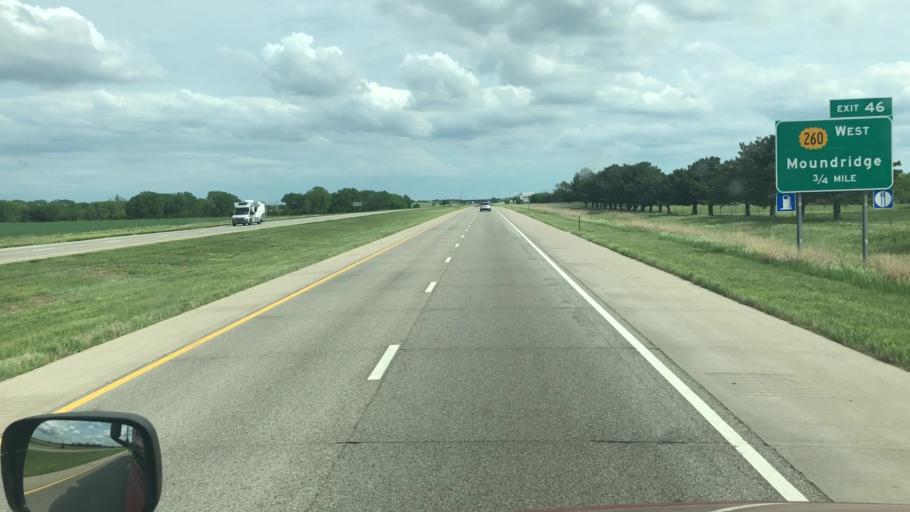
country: US
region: Kansas
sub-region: McPherson County
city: Moundridge
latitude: 38.2140
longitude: -97.4982
